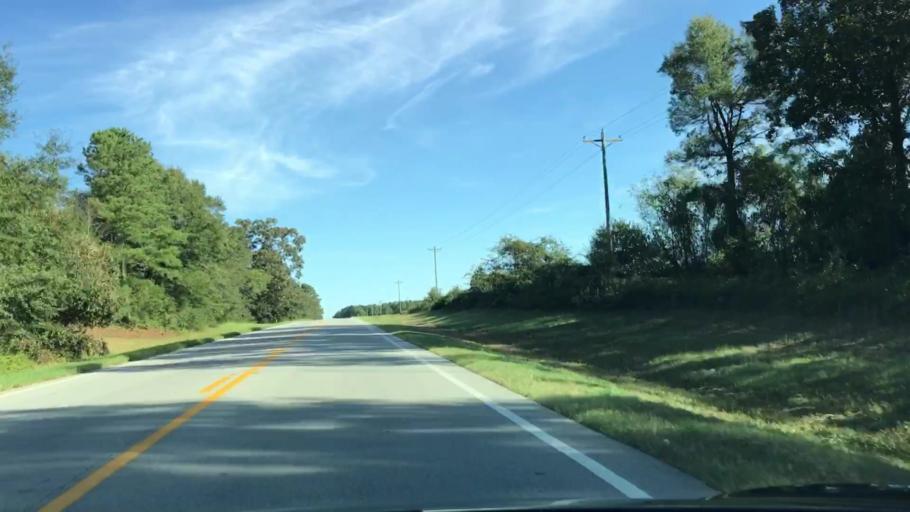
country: US
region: Georgia
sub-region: Glascock County
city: Gibson
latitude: 33.3147
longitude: -82.5436
